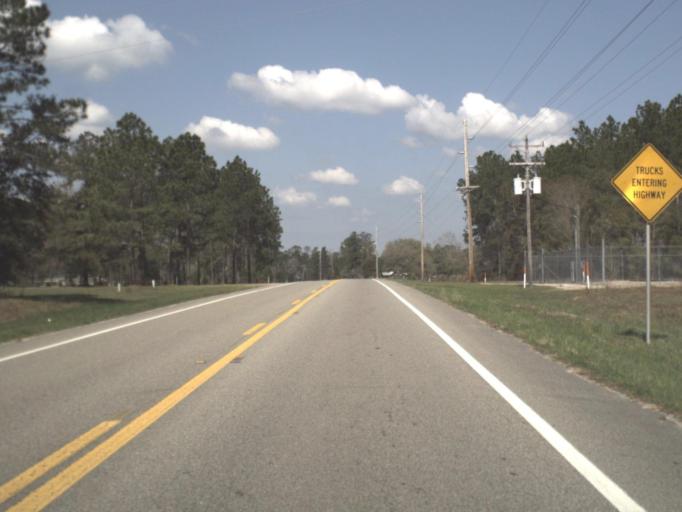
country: US
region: Florida
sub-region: Liberty County
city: Bristol
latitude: 30.4008
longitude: -84.8145
